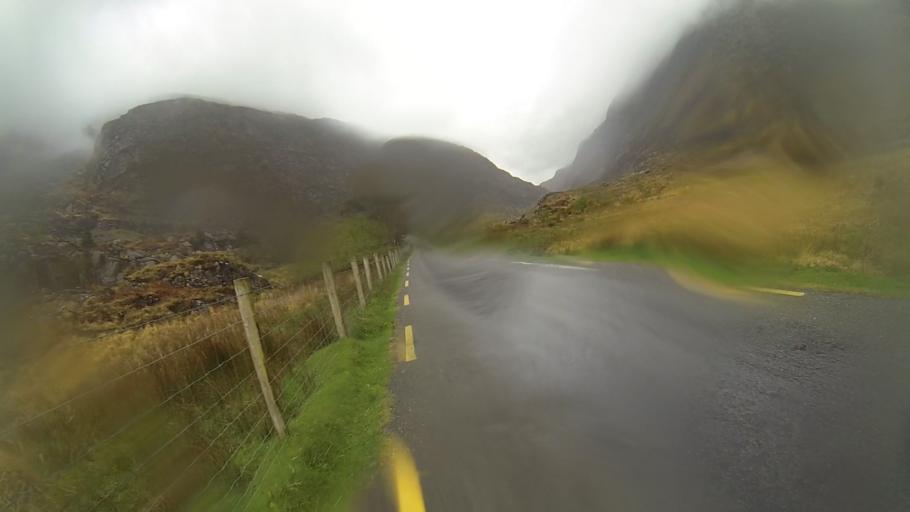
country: IE
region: Munster
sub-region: Ciarrai
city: Cill Airne
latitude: 52.0177
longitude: -9.6358
